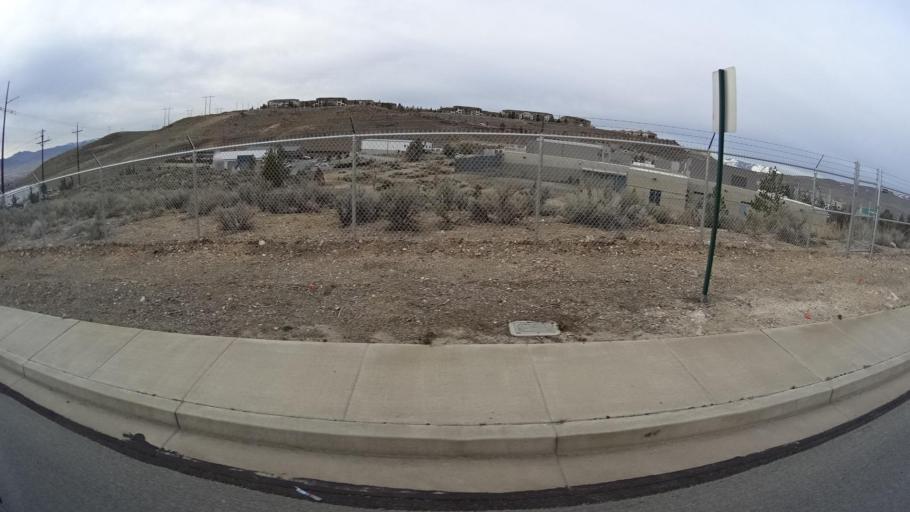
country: US
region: Nevada
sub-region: Washoe County
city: Sun Valley
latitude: 39.5708
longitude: -119.8079
